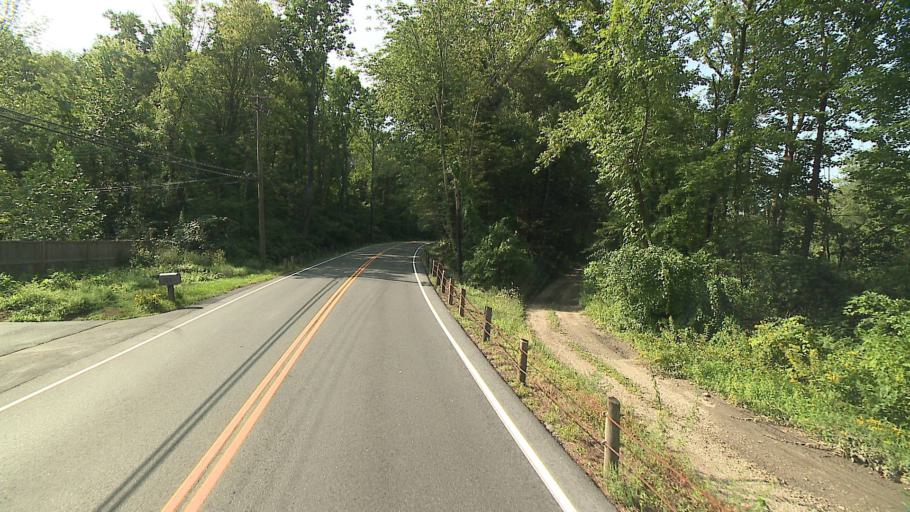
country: US
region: Connecticut
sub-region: Litchfield County
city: Kent
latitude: 41.6835
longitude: -73.5059
